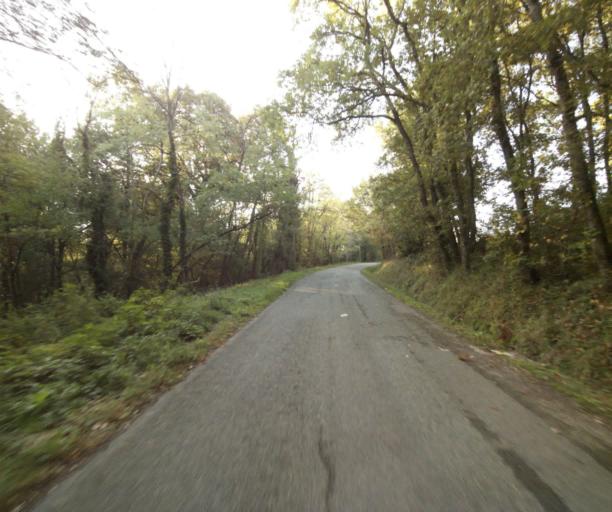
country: FR
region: Midi-Pyrenees
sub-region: Departement du Tarn-et-Garonne
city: Saint-Nauphary
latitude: 43.9370
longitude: 1.4414
